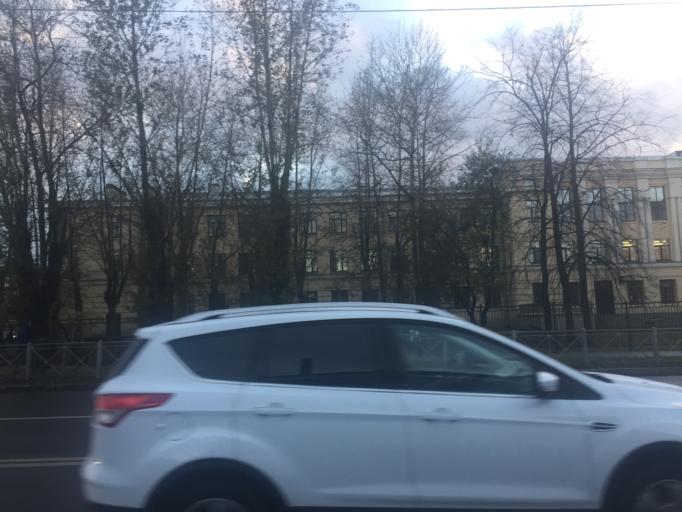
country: RU
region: St.-Petersburg
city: Obukhovo
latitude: 59.8789
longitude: 30.4406
